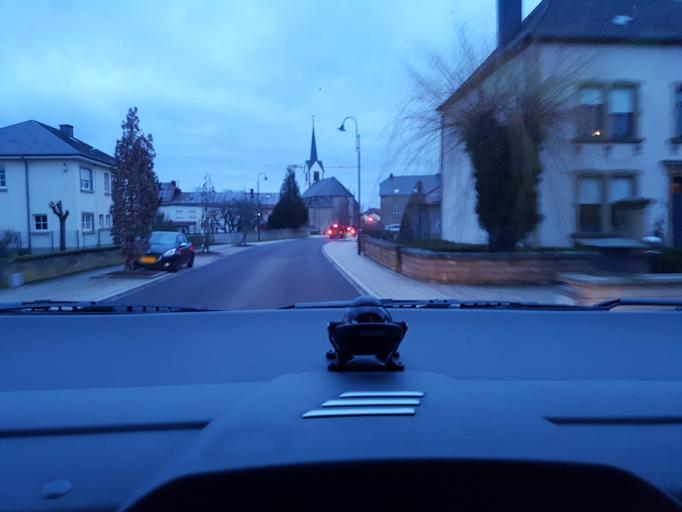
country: LU
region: Grevenmacher
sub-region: Canton de Remich
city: Mondorf-les-Bains
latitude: 49.5047
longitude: 6.3172
